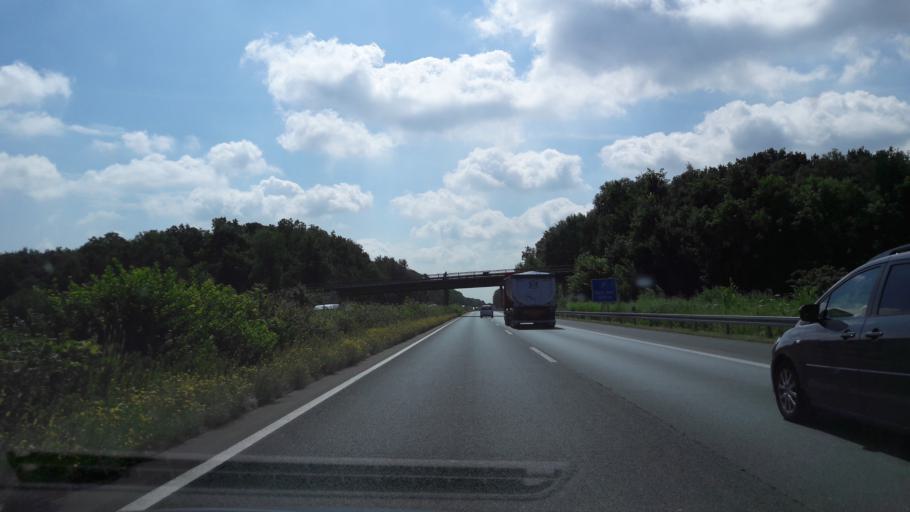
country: DE
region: North Rhine-Westphalia
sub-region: Regierungsbezirk Munster
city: Ascheberg
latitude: 51.8227
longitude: 7.6088
